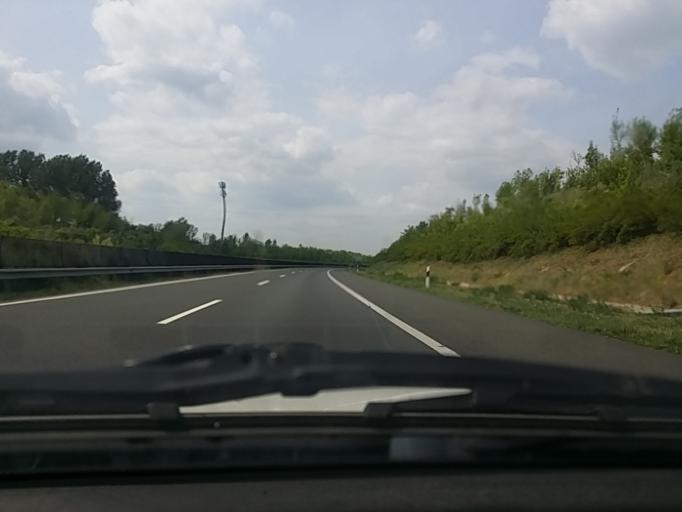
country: HU
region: Somogy
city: Balatonlelle
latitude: 46.7673
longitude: 17.7092
